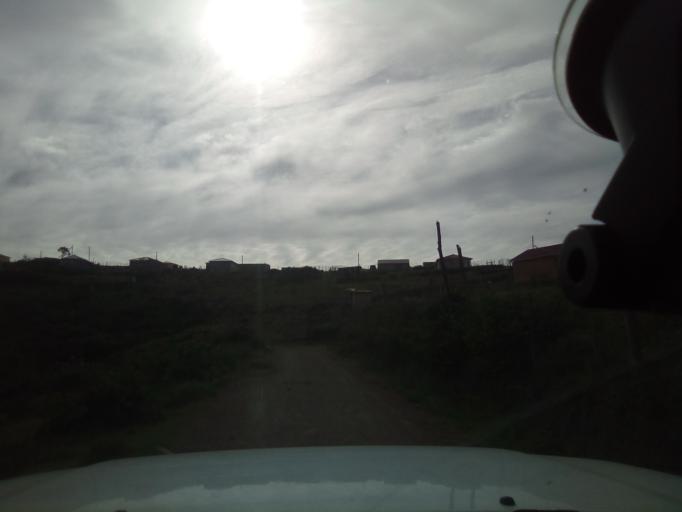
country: ZA
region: Eastern Cape
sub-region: Buffalo City Metropolitan Municipality
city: East London
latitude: -32.7958
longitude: 27.9672
